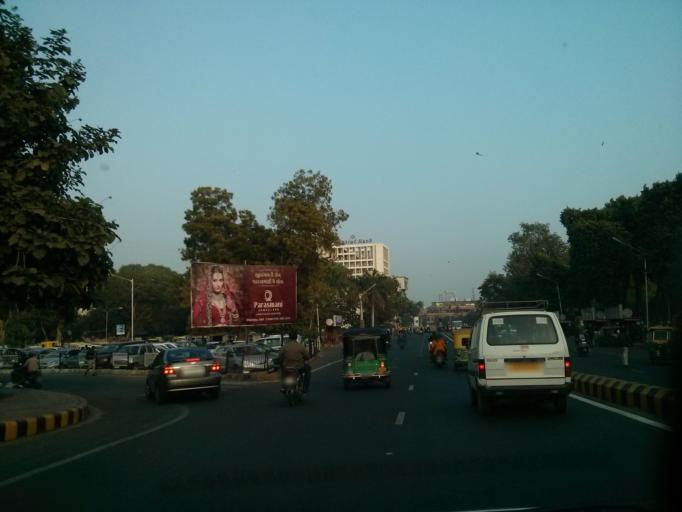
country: IN
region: Gujarat
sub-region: Ahmadabad
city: Ahmedabad
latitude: 23.0272
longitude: 72.5778
